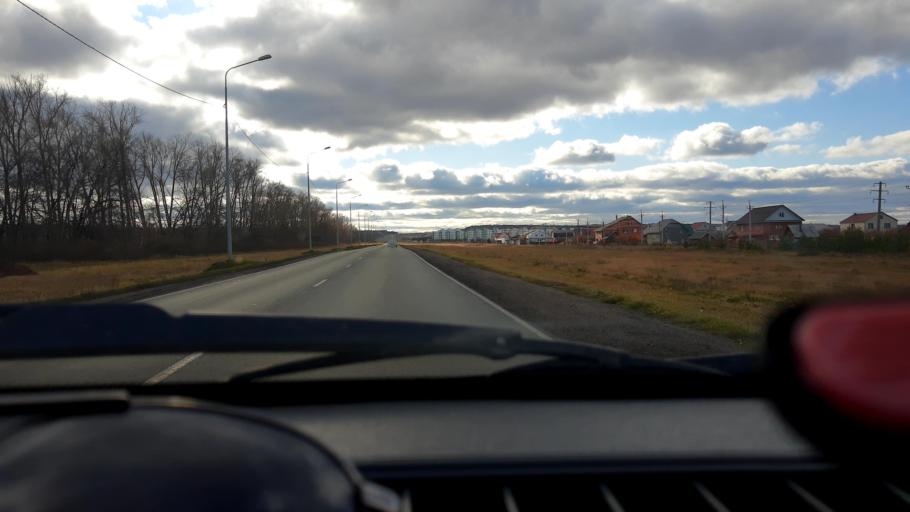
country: RU
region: Bashkortostan
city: Avdon
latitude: 54.4901
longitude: 55.8993
